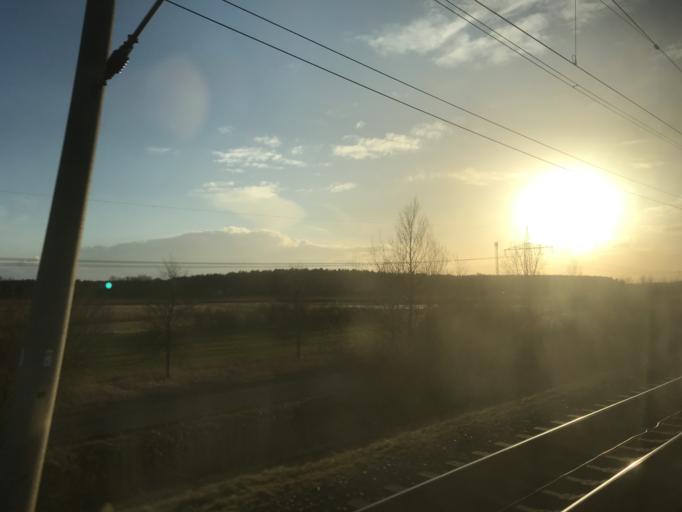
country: DE
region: Saxony-Anhalt
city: Stendal
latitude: 52.5764
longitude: 11.8839
